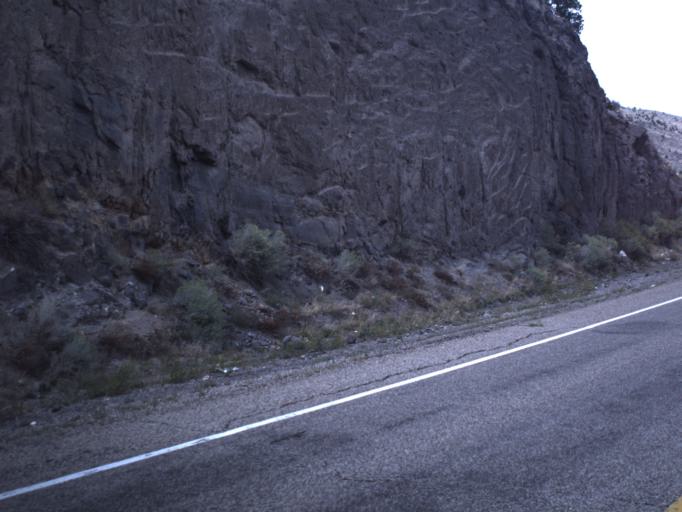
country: US
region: Utah
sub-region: Piute County
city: Junction
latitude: 38.1316
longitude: -112.3165
